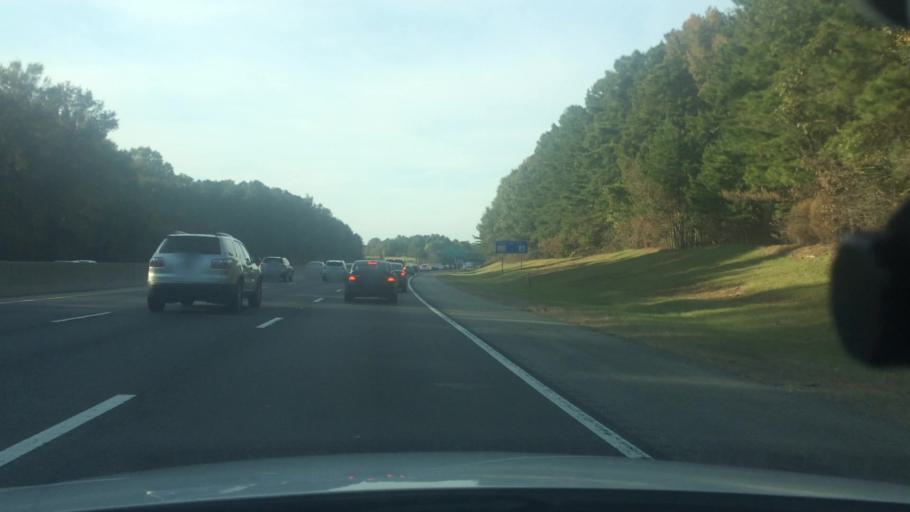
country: US
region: North Carolina
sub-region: Orange County
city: Chapel Hill
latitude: 35.9082
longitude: -78.9770
